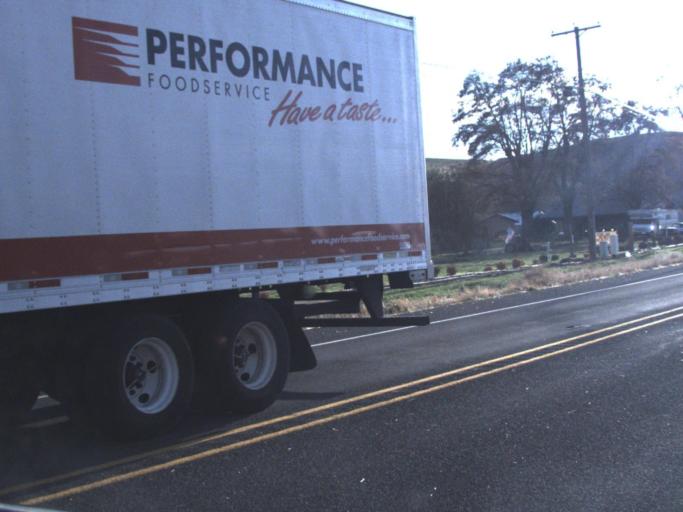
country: US
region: Washington
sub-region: Columbia County
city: Dayton
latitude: 46.2945
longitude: -118.0223
